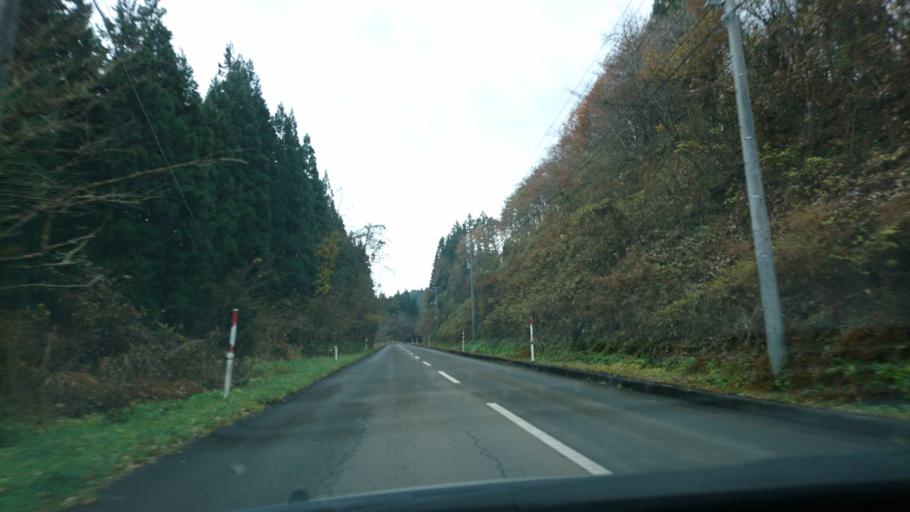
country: JP
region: Iwate
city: Ichinoseki
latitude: 38.9710
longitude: 140.9404
